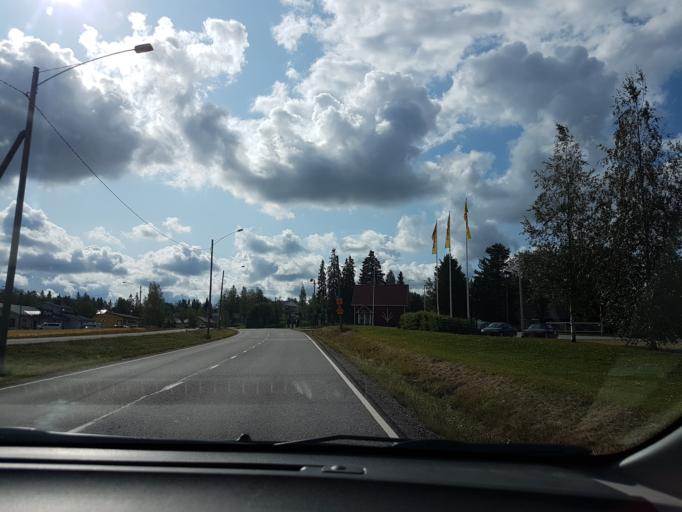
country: FI
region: Uusimaa
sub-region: Helsinki
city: Pornainen
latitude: 60.4812
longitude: 25.3712
